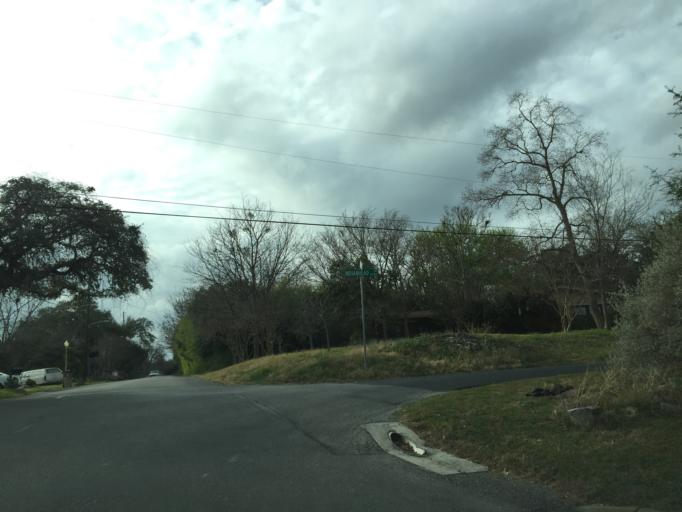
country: US
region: Texas
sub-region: Travis County
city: Wells Branch
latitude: 30.3837
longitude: -97.6784
